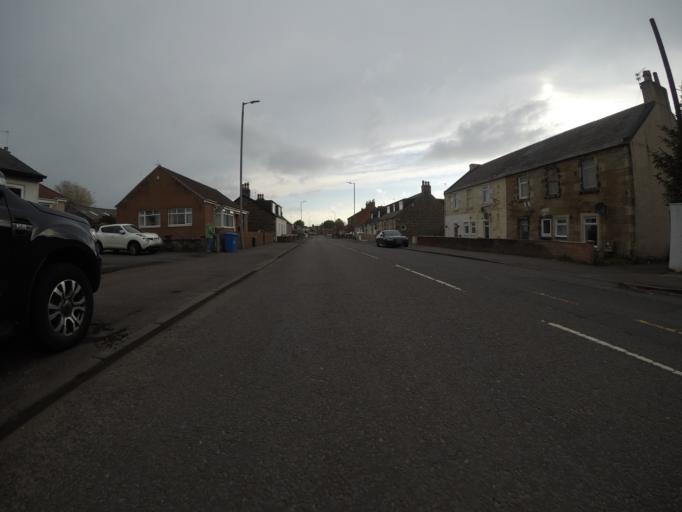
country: GB
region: Scotland
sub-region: North Ayrshire
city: Dreghorn
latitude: 55.6083
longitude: -4.6205
